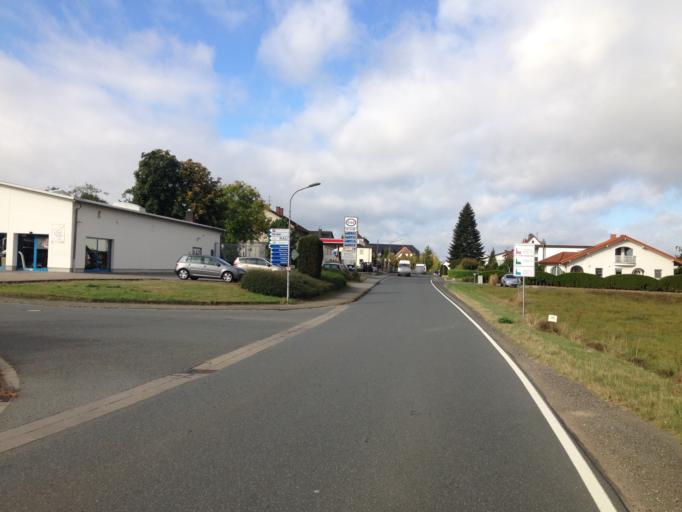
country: DE
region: Hesse
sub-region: Regierungsbezirk Giessen
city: Bad Endbach
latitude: 50.6753
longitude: 8.5334
